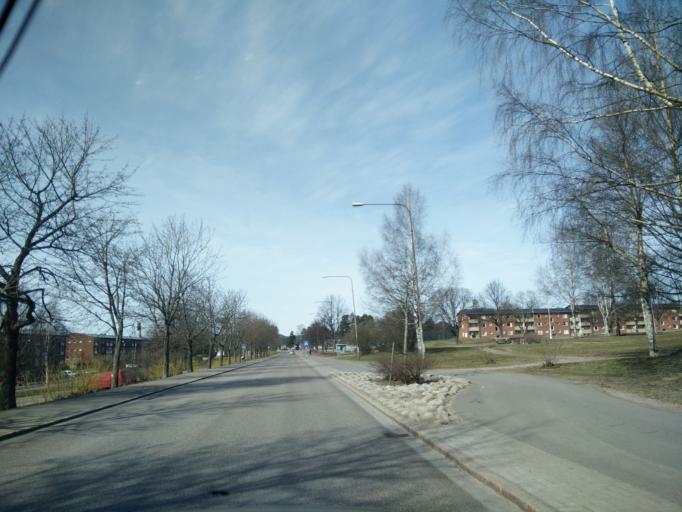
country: SE
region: Vaermland
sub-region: Hagfors Kommun
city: Hagfors
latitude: 60.0374
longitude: 13.6931
